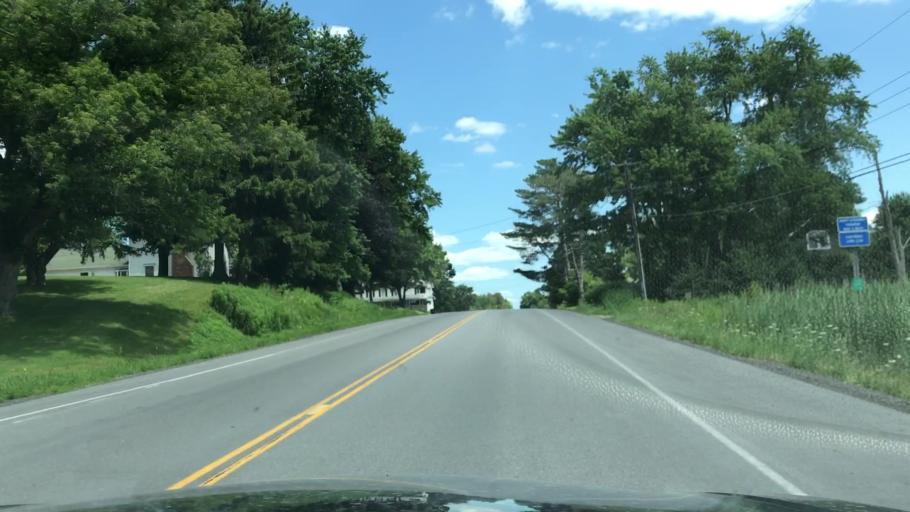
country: US
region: New York
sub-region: Erie County
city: Alden
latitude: 42.7697
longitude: -78.4441
